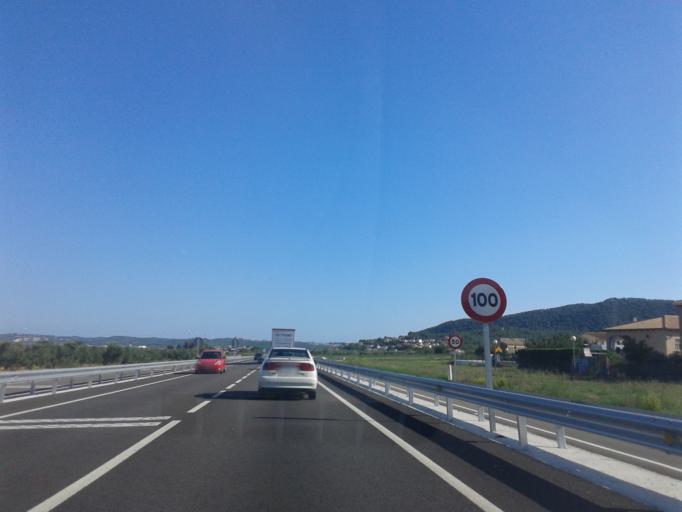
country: ES
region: Catalonia
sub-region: Provincia de Tarragona
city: Albinyana
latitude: 41.2545
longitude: 1.5060
